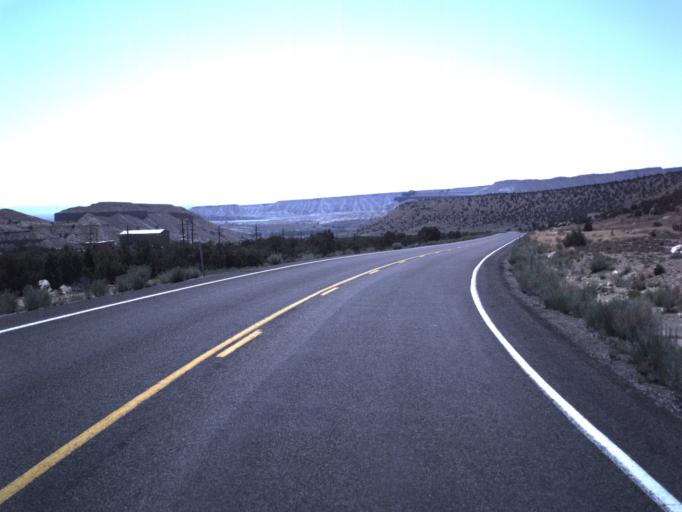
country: US
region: Utah
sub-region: Emery County
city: Orangeville
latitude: 39.2773
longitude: -111.1009
